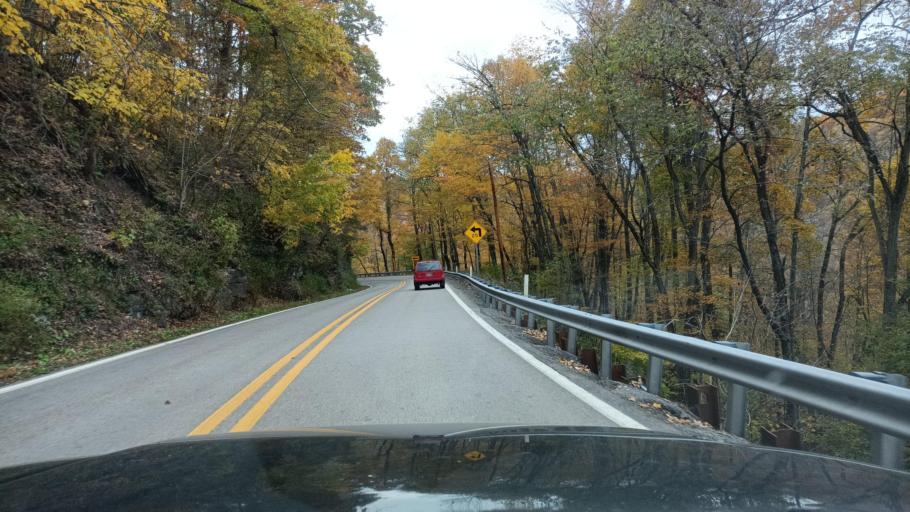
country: US
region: West Virginia
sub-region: Preston County
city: Terra Alta
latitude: 39.2992
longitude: -79.6062
